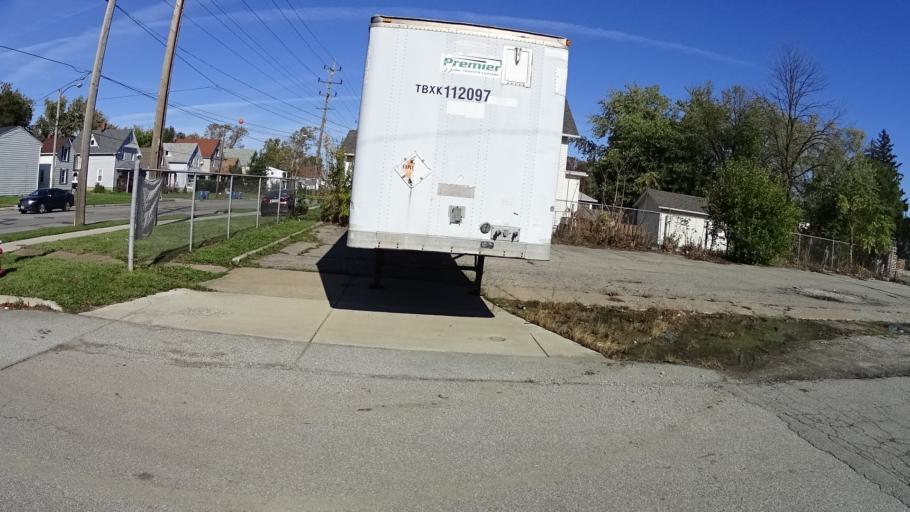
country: US
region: Ohio
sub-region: Lorain County
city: Lorain
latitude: 41.4570
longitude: -82.1849
